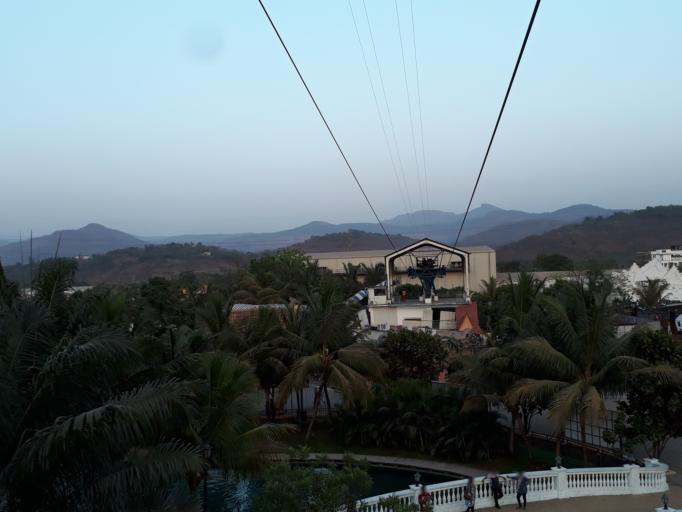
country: IN
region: Maharashtra
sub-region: Raigarh
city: Khopoli
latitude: 18.7676
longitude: 73.2809
